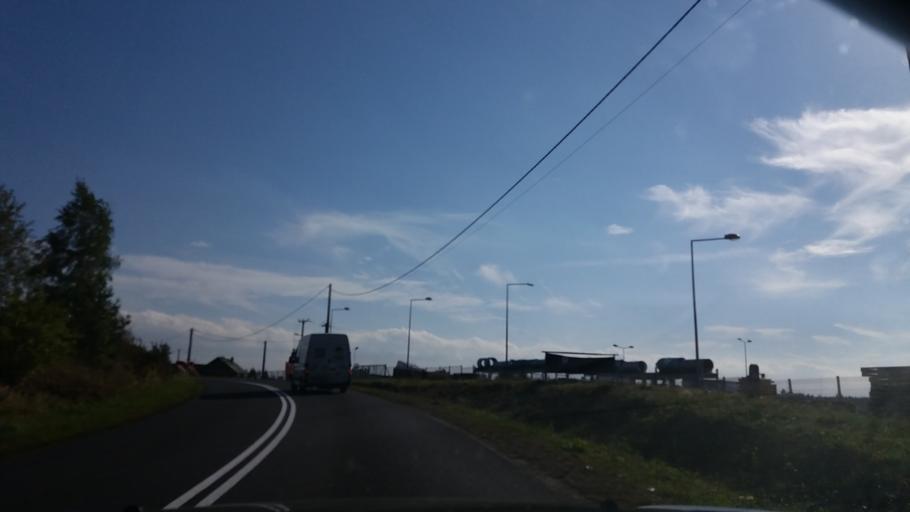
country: PL
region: Lesser Poland Voivodeship
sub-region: Powiat chrzanowski
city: Grojec
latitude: 50.0971
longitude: 19.5536
